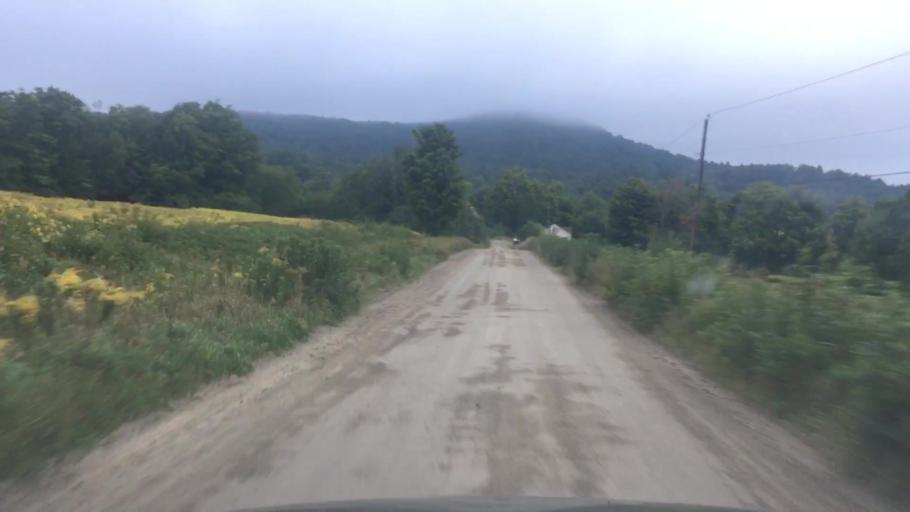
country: US
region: Vermont
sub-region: Windham County
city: Dover
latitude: 42.8552
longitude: -72.7789
